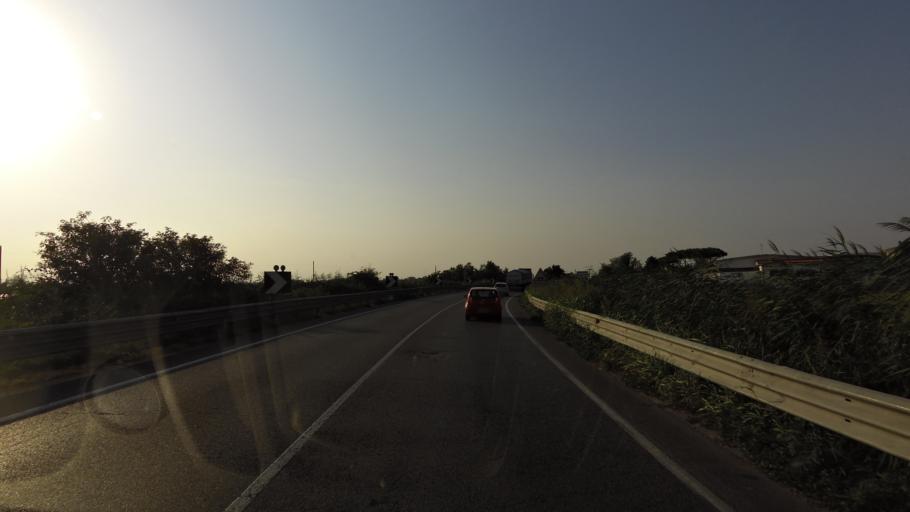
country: IT
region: Emilia-Romagna
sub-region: Provincia di Ferrara
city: Porto Garibaldi
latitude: 44.6788
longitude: 12.2246
